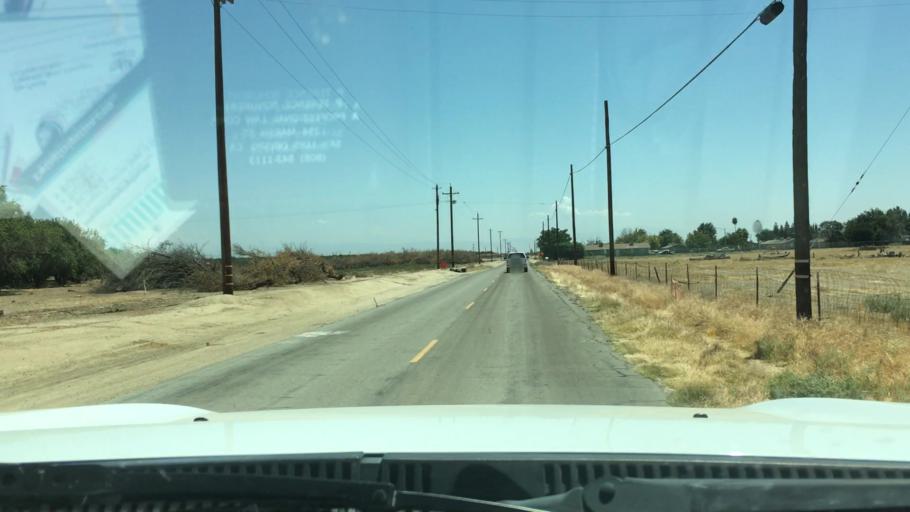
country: US
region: California
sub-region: Kern County
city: Shafter
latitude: 35.5291
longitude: -119.3112
